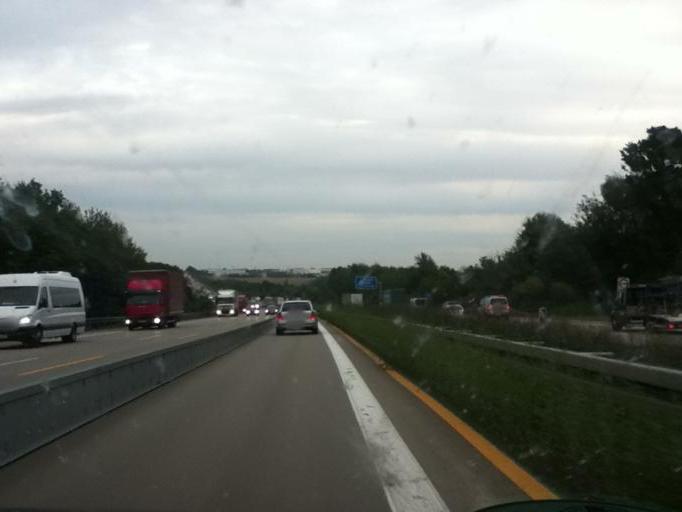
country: DE
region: Saxony
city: Wilsdruff
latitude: 51.0607
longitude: 13.5167
